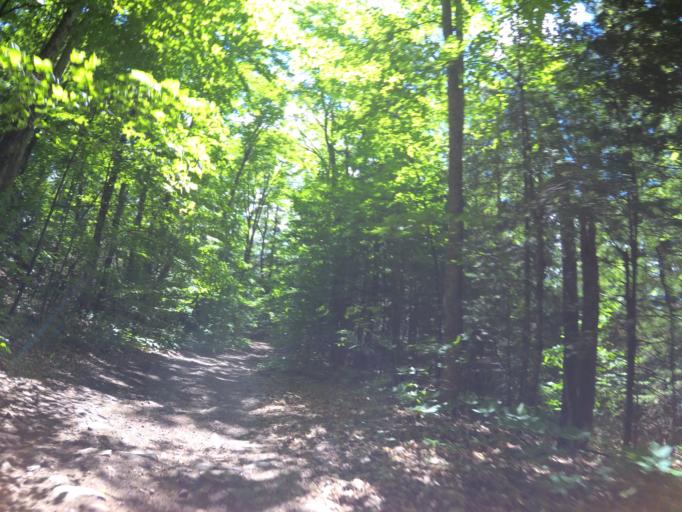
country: CA
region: Ontario
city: Renfrew
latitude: 45.0498
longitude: -76.8368
